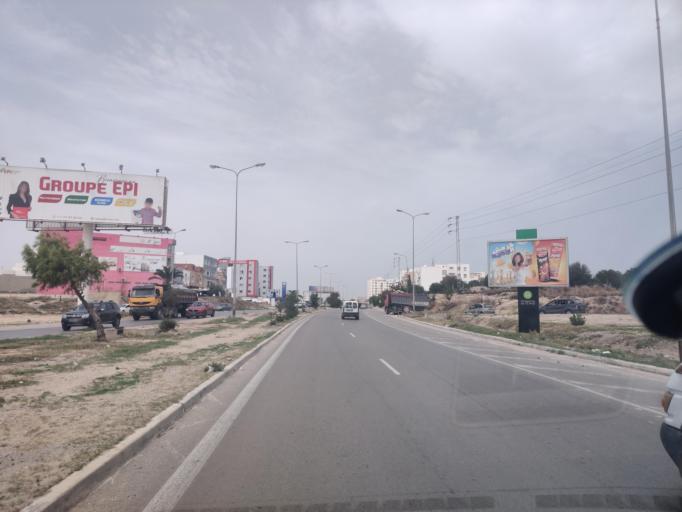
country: TN
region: Susah
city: Hammam Sousse
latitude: 35.8276
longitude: 10.5910
